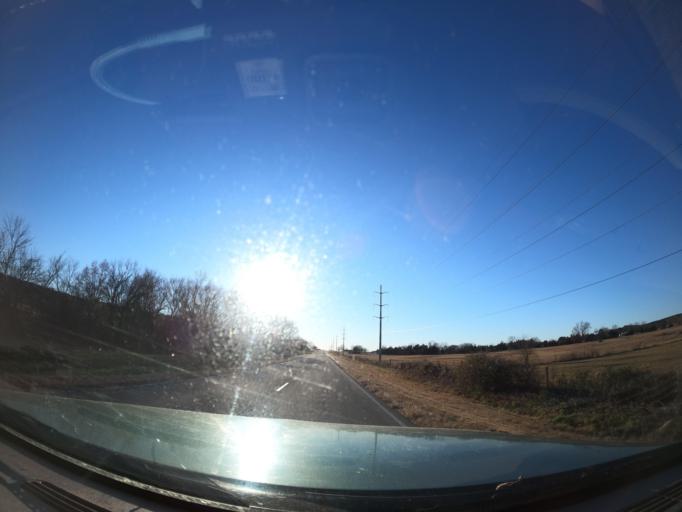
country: US
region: Oklahoma
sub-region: Pittsburg County
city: Hartshorne
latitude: 34.8807
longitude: -95.4987
